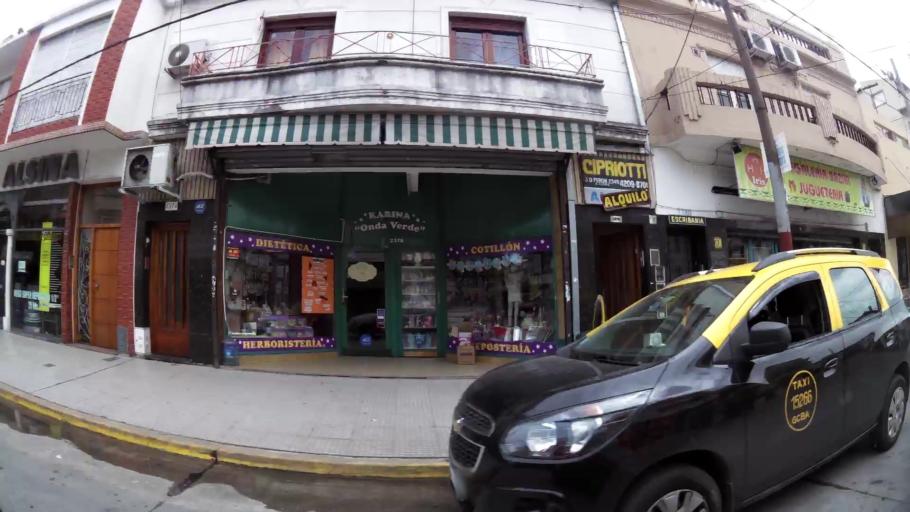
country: AR
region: Buenos Aires
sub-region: Partido de Lanus
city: Lanus
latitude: -34.6752
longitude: -58.4039
